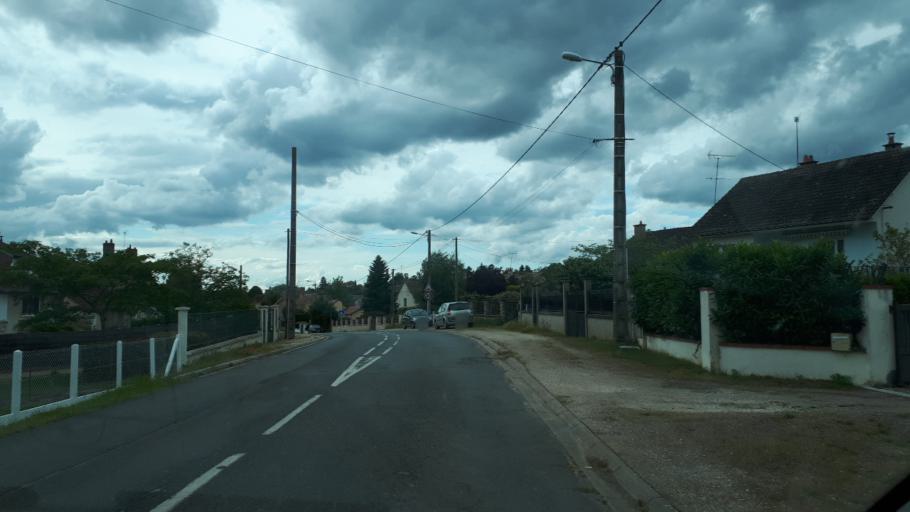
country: FR
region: Centre
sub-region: Departement du Cher
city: Gracay
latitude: 47.1414
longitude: 1.8559
